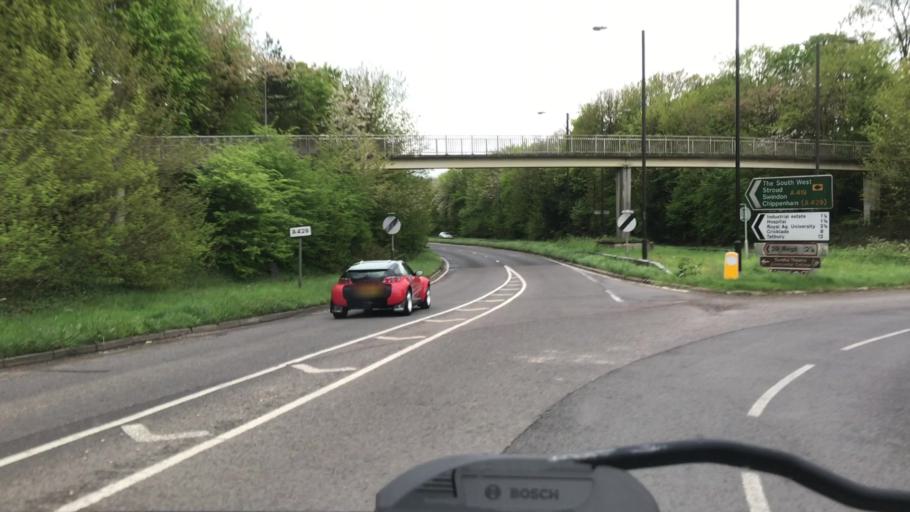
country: GB
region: England
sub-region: Gloucestershire
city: Cirencester
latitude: 51.7175
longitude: -1.9593
